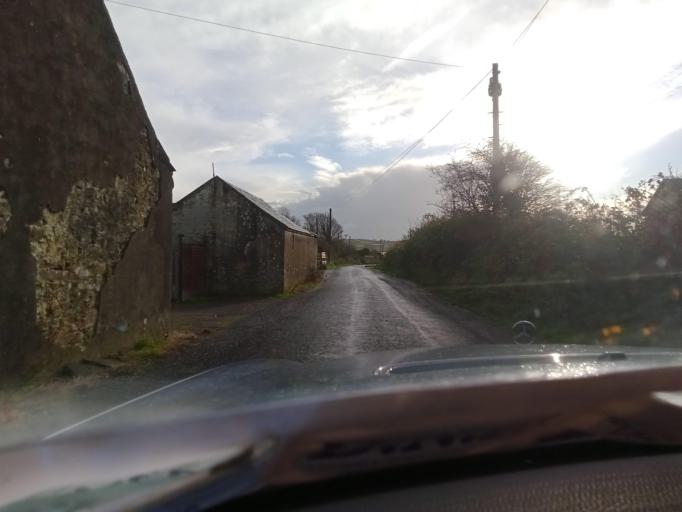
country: IE
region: Leinster
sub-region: Kilkenny
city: Mooncoin
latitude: 52.2770
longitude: -7.1860
